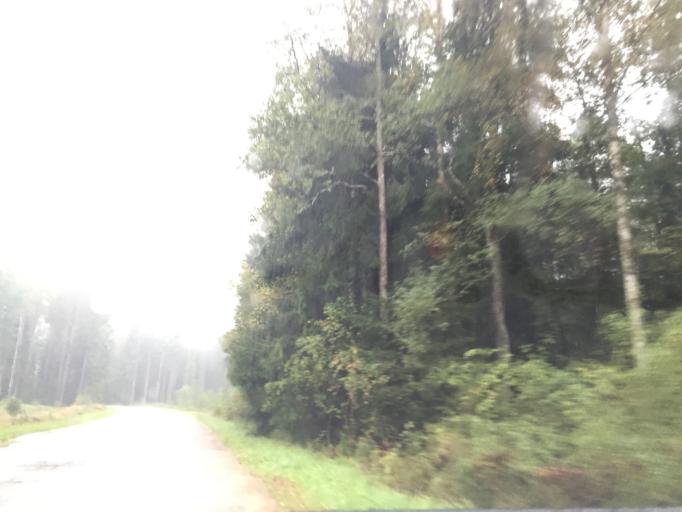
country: LV
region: Ropazu
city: Ropazi
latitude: 57.0095
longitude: 24.6809
